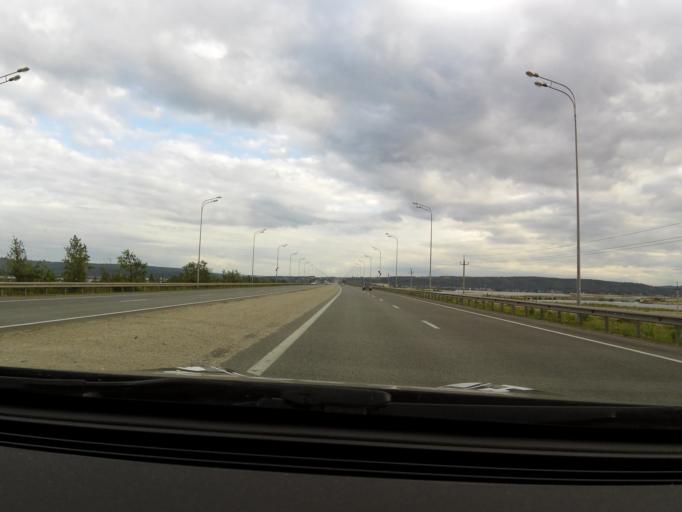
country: RU
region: Tatarstan
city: Osinovo
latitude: 55.8133
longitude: 48.8420
